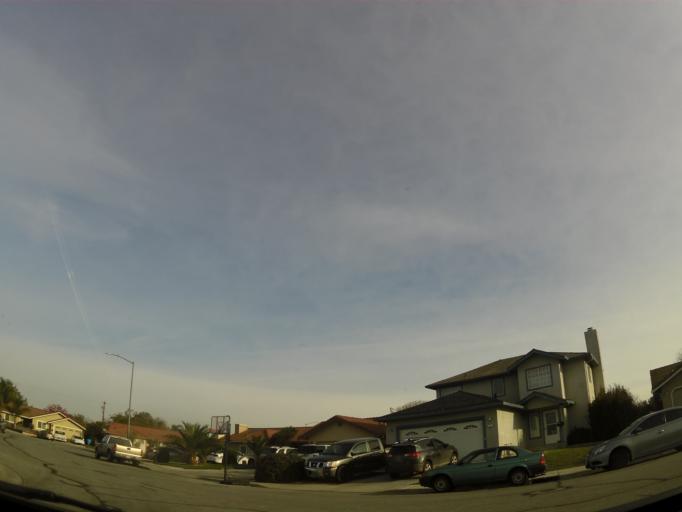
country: US
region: California
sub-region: San Benito County
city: Hollister
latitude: 36.8641
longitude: -121.4204
